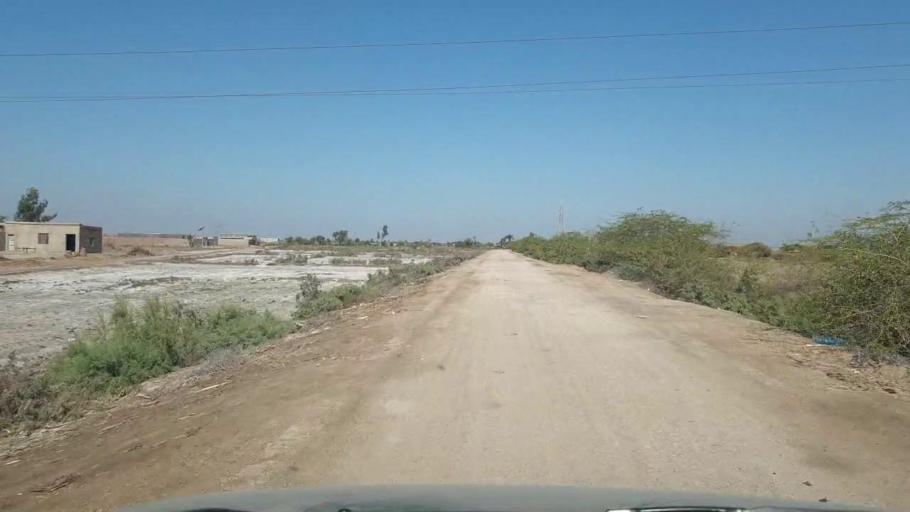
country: PK
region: Sindh
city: Mirwah Gorchani
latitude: 25.3104
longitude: 69.1287
